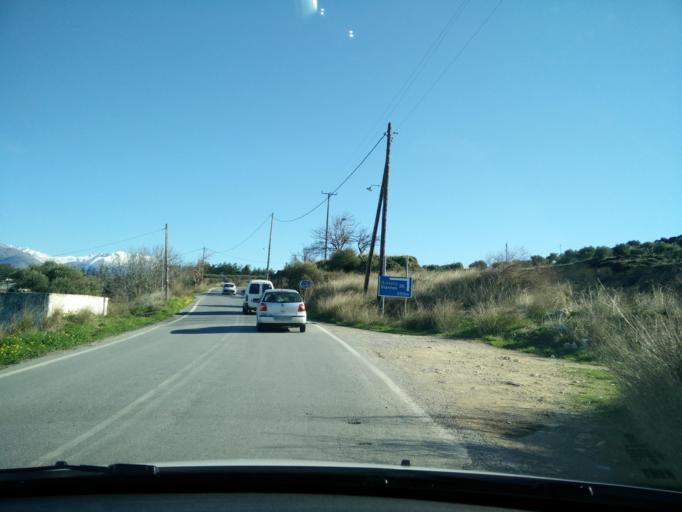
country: GR
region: Crete
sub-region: Nomos Irakleiou
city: Arkalochori
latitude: 35.1357
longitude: 25.2632
